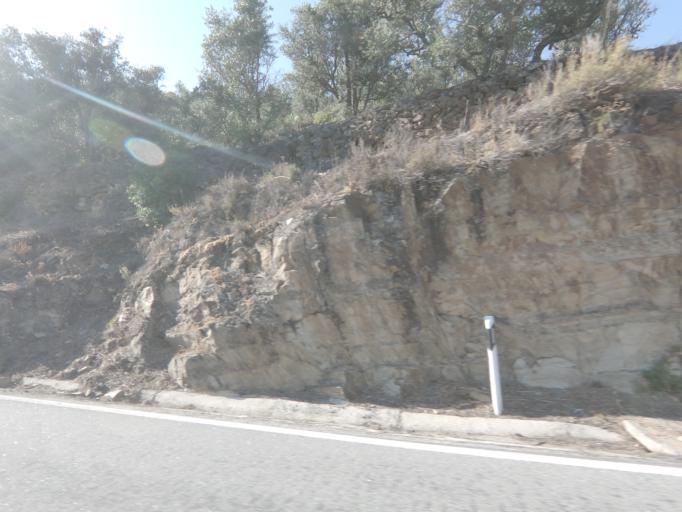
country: PT
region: Viseu
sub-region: Tabuaco
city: Tabuaco
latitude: 41.1249
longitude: -7.5706
